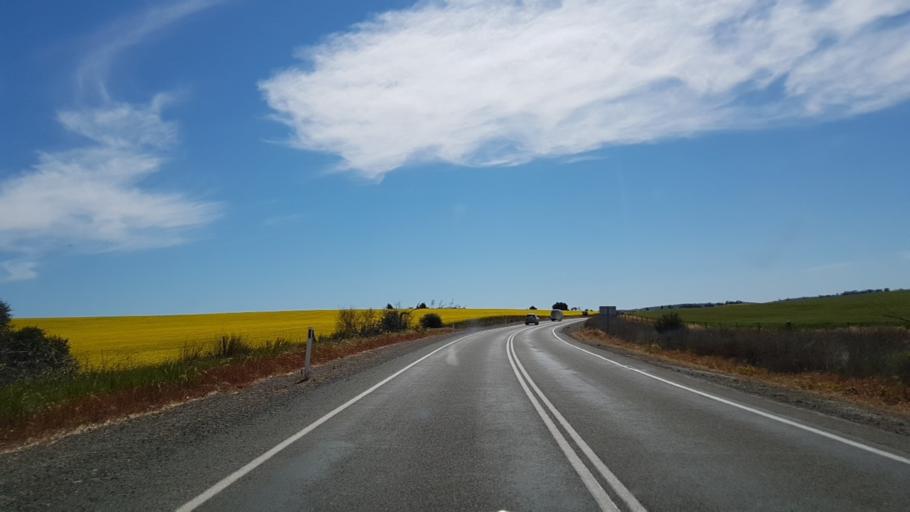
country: AU
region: South Australia
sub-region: Clare and Gilbert Valleys
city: Clare
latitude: -34.0703
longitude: 138.7886
